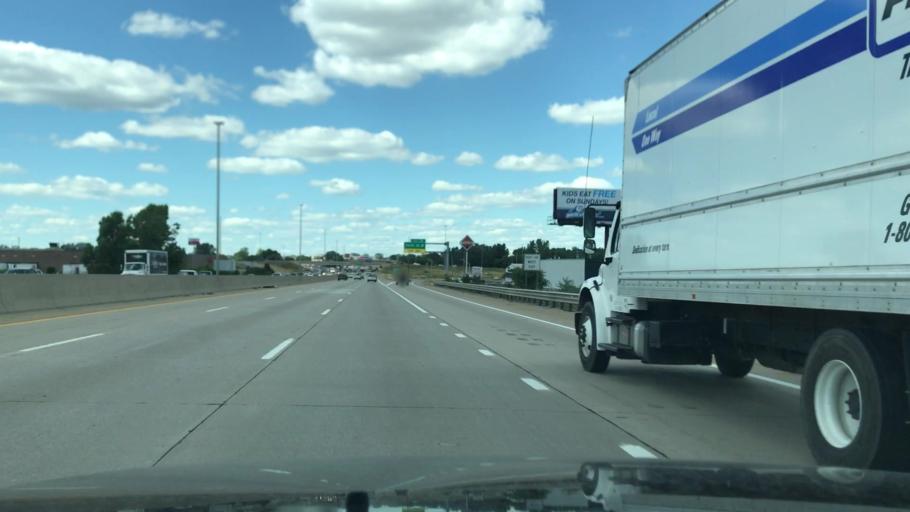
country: US
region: Michigan
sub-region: Kent County
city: Cutlerville
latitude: 42.8604
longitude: -85.6791
